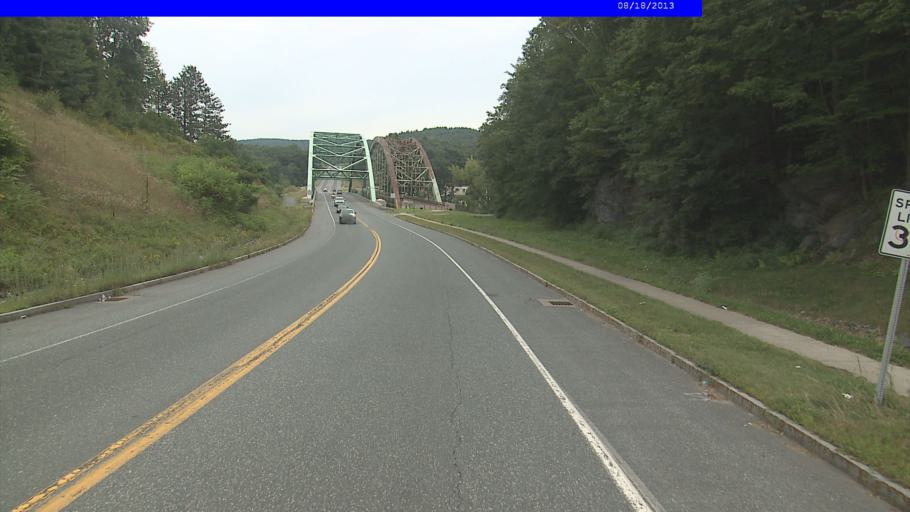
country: US
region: Vermont
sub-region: Windham County
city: Brattleboro
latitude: 42.8840
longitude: -72.5542
